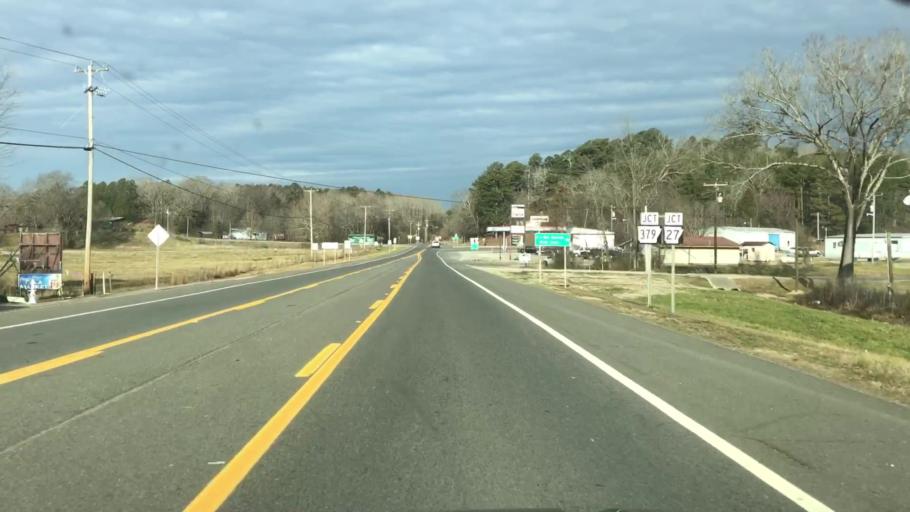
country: US
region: Arkansas
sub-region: Montgomery County
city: Mount Ida
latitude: 34.5612
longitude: -93.6377
